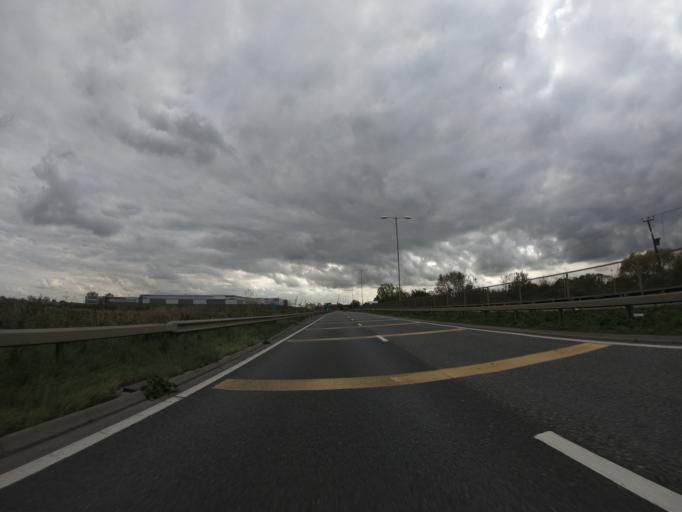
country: GB
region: England
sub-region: Borough of Thurrock
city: Tilbury
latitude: 51.4725
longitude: 0.3484
